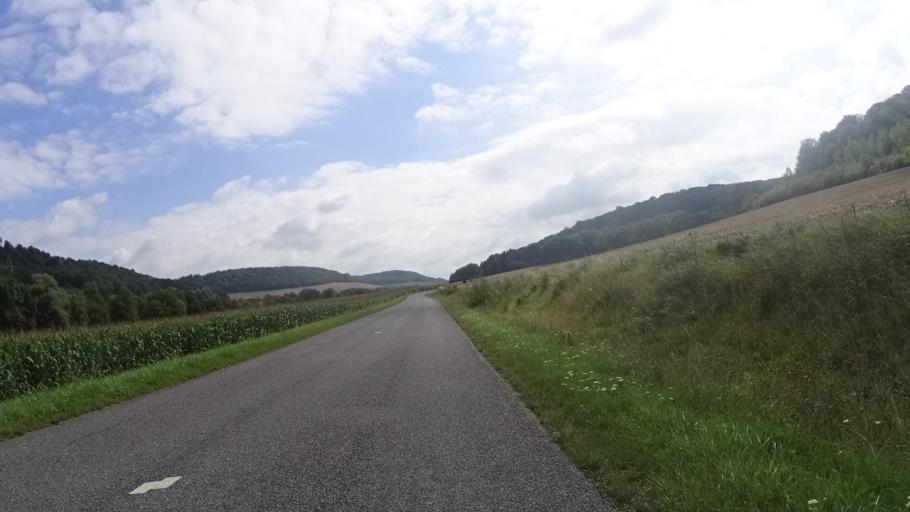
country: FR
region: Lorraine
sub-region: Departement de la Meuse
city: Velaines
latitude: 48.7183
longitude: 5.3268
